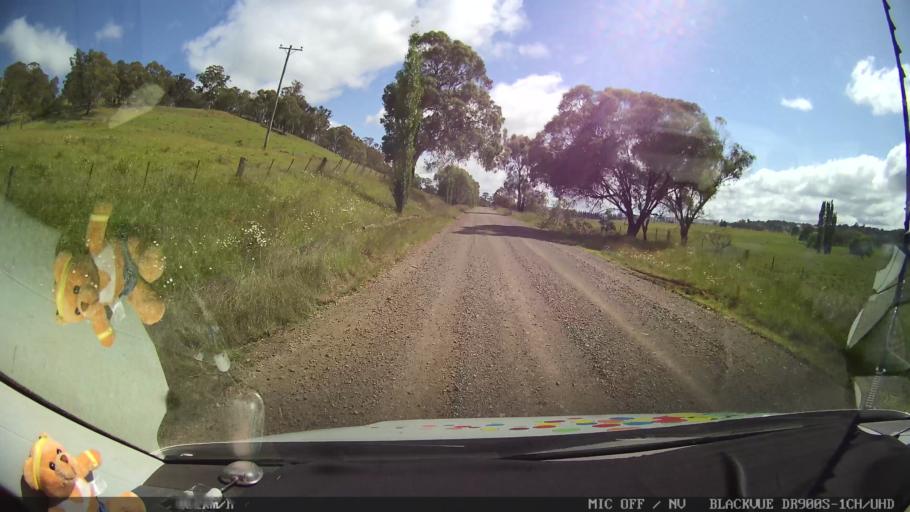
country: AU
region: New South Wales
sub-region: Glen Innes Severn
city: Glen Innes
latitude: -29.9559
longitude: 151.7034
